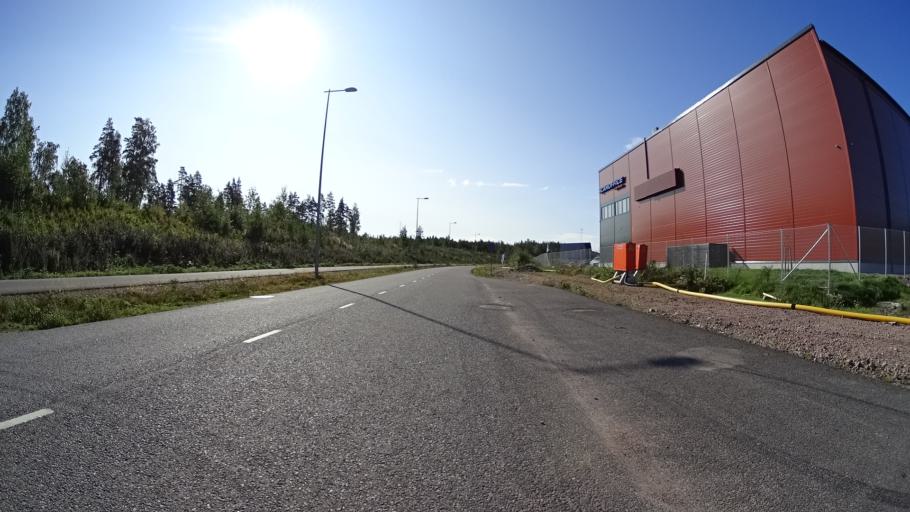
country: FI
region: Uusimaa
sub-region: Helsinki
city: Kilo
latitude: 60.2954
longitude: 24.7678
